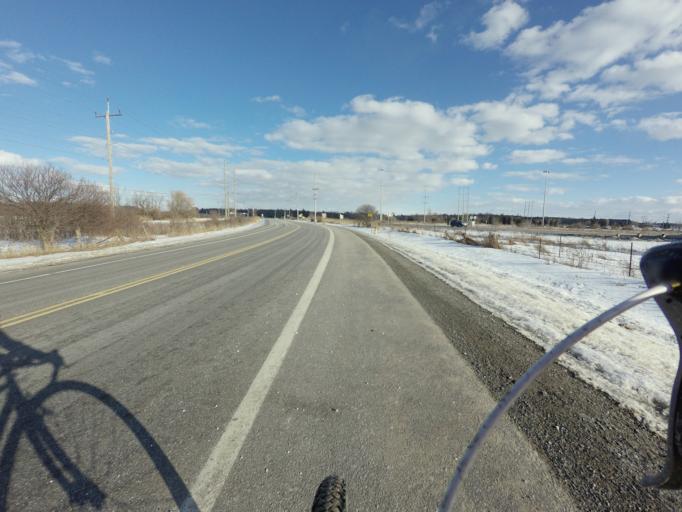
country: CA
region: Ontario
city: Bells Corners
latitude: 45.3231
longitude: -75.8849
